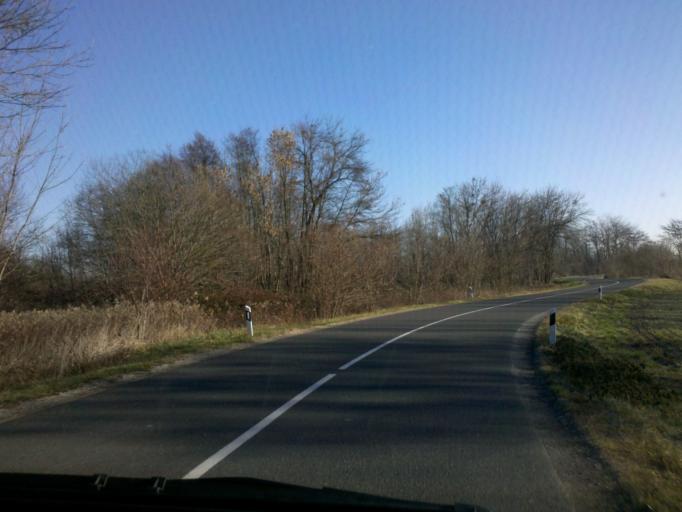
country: HR
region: Medimurska
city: Domasinec
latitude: 46.4104
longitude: 16.6112
